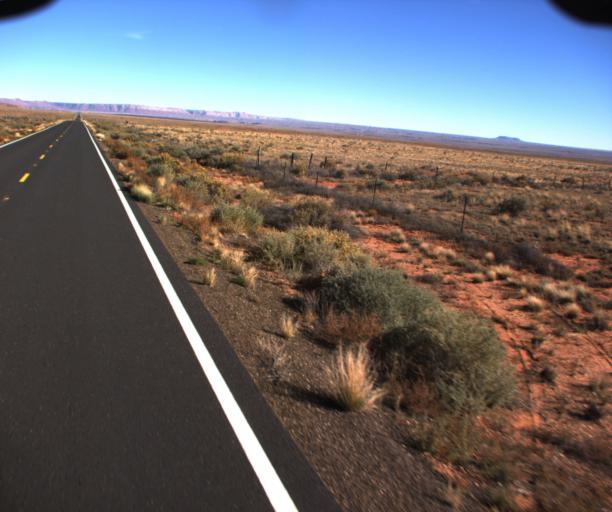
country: US
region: Arizona
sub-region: Coconino County
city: Page
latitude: 36.7065
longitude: -111.9538
